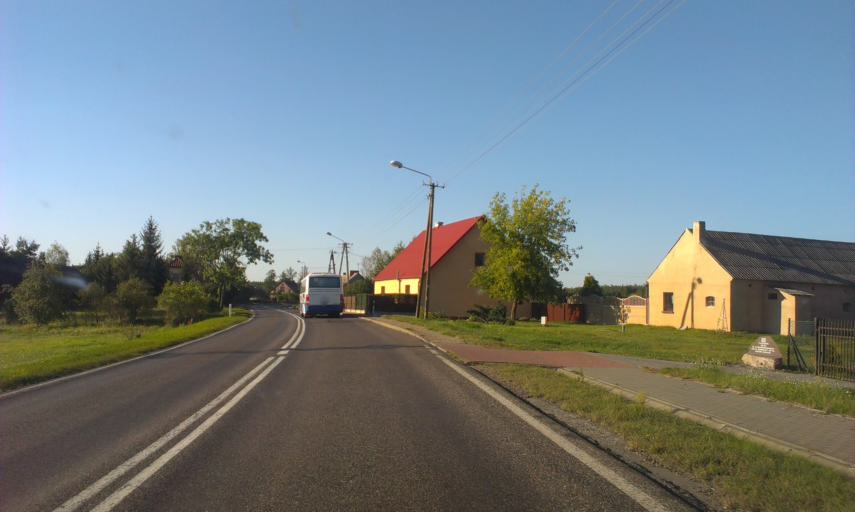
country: PL
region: Kujawsko-Pomorskie
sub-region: Powiat tucholski
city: Cekcyn
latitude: 53.5297
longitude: 17.9463
